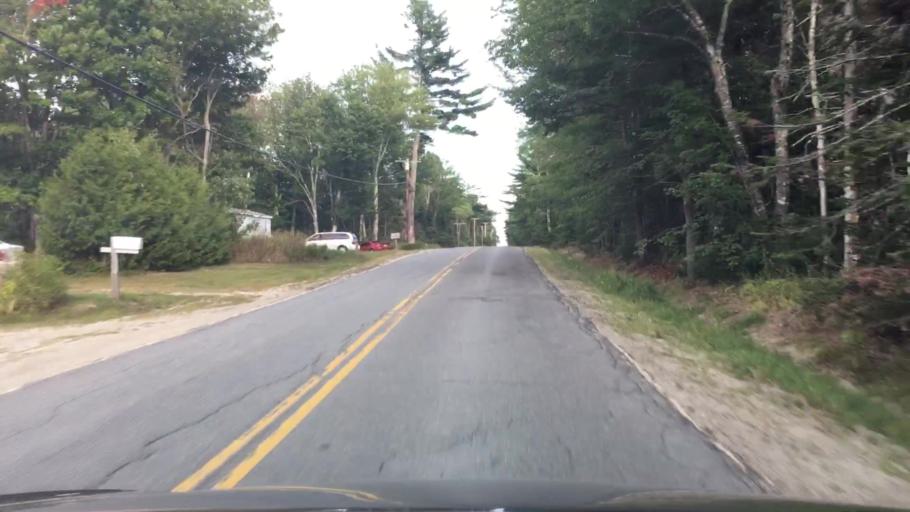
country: US
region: Maine
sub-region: Hancock County
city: Surry
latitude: 44.5002
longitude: -68.5632
